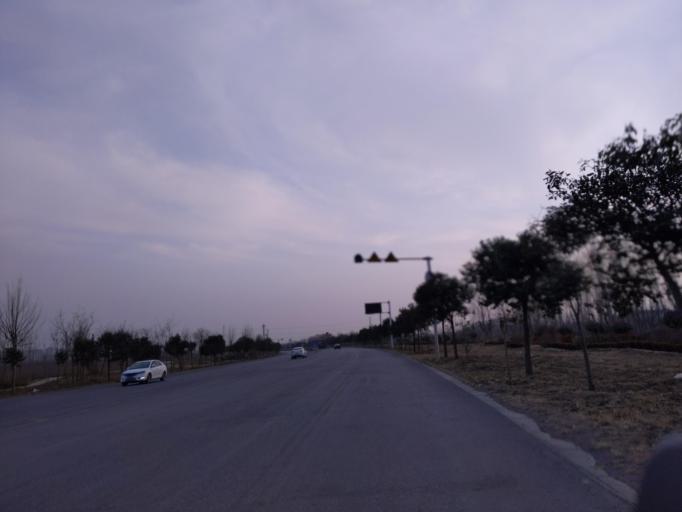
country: CN
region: Henan Sheng
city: Puyang
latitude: 35.8132
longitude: 114.9668
